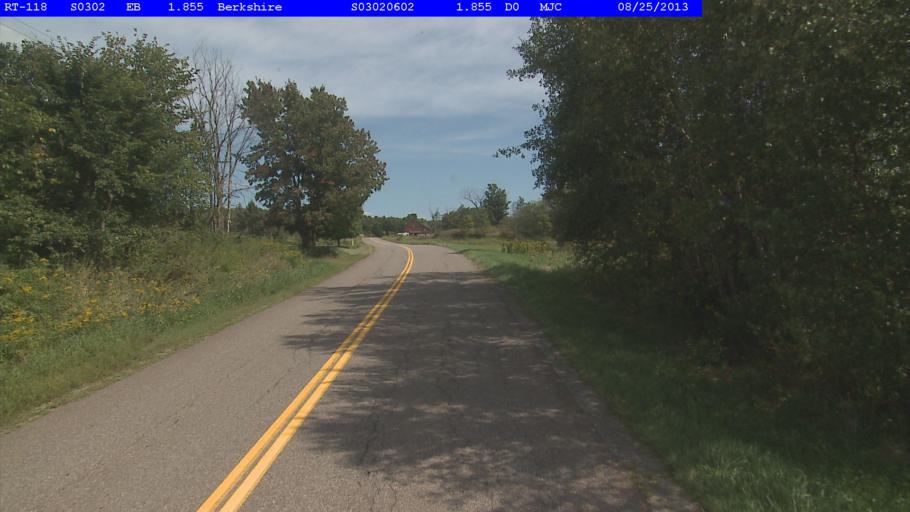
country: US
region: Vermont
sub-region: Franklin County
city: Enosburg Falls
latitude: 44.9783
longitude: -72.7800
